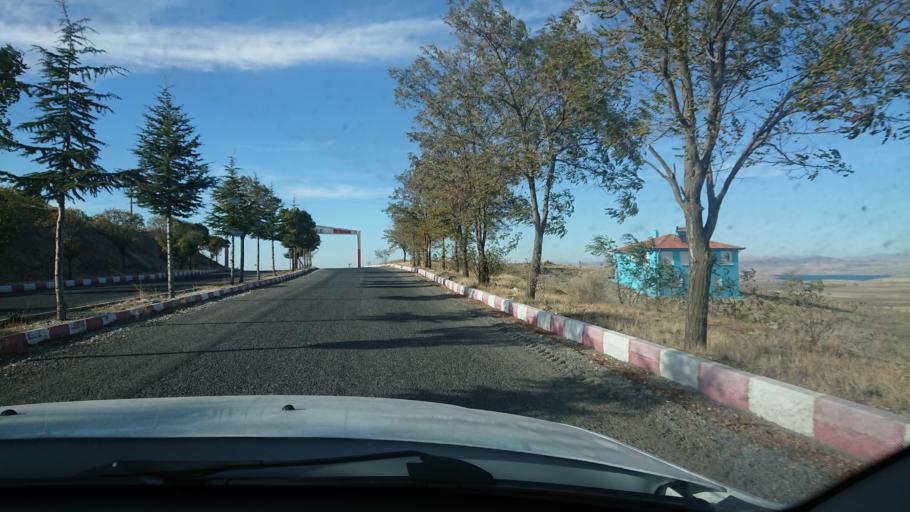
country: TR
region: Aksaray
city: Sariyahsi
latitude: 38.9672
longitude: 33.8728
